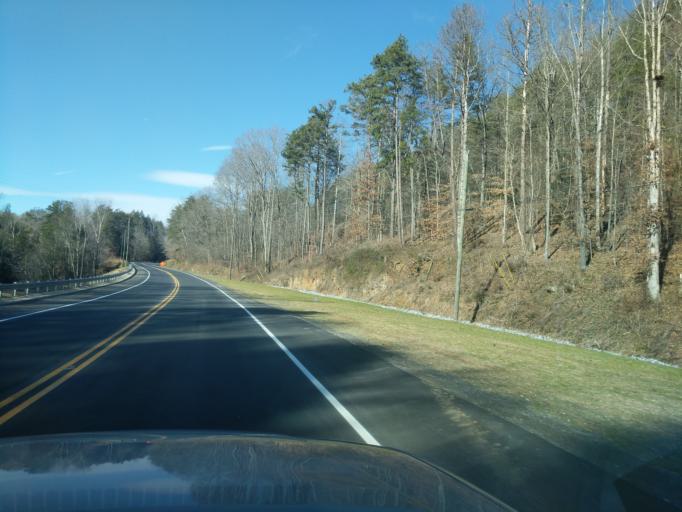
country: US
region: North Carolina
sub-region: McDowell County
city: West Marion
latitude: 35.5759
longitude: -81.9764
